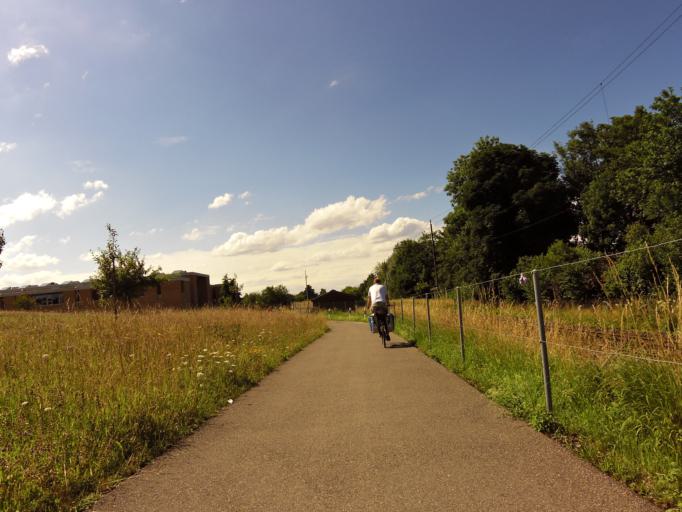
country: CH
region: Thurgau
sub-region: Arbon District
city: Arbon
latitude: 47.5277
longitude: 9.4157
